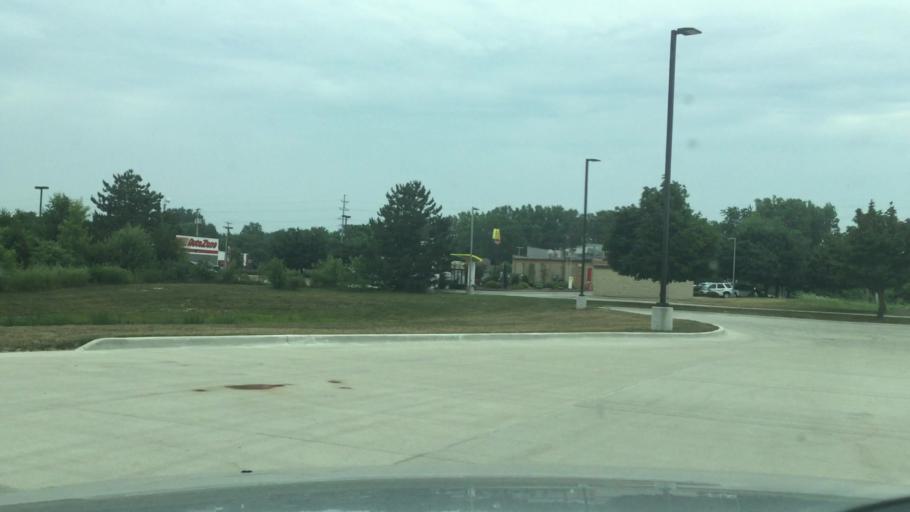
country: US
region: Michigan
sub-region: Genesee County
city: Flint
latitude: 42.9754
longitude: -83.7116
